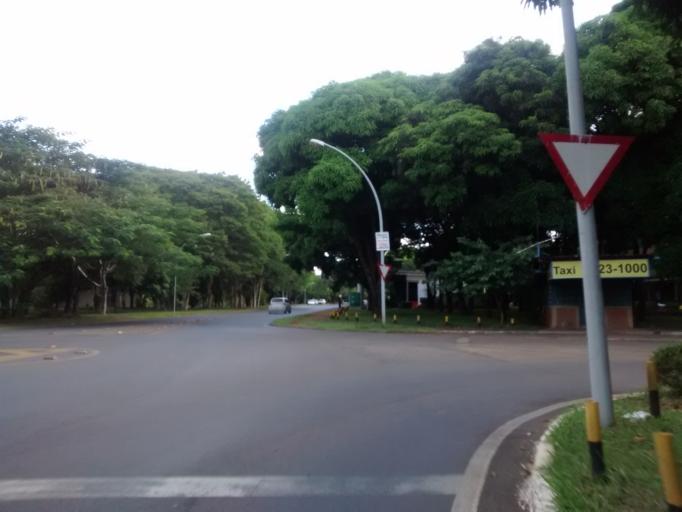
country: BR
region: Federal District
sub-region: Brasilia
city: Brasilia
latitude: -15.8022
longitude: -47.8908
